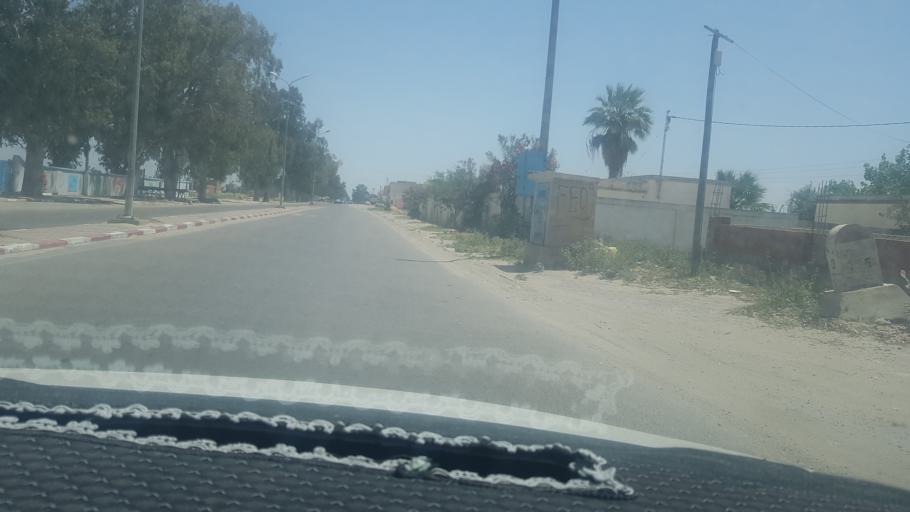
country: TN
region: Al Qayrawan
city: Kairouan
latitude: 35.6168
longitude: 9.9292
